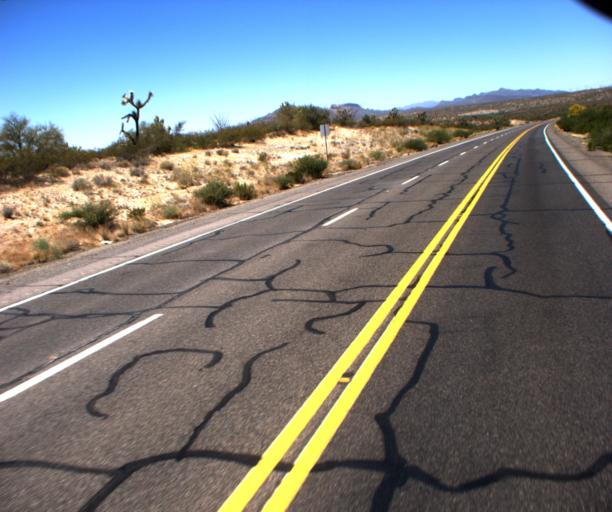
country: US
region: Arizona
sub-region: Yavapai County
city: Congress
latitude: 34.1923
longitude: -113.0547
